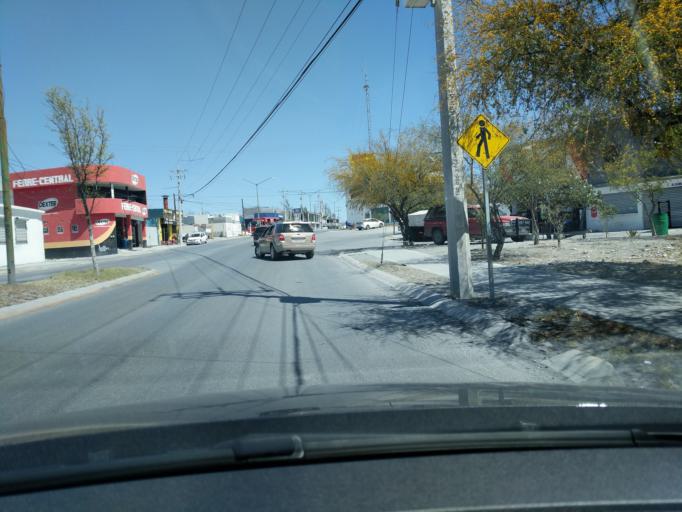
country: MX
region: Nuevo Leon
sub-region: Pesqueria
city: Colinas del Aeropuerto
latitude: 25.8167
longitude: -100.1085
